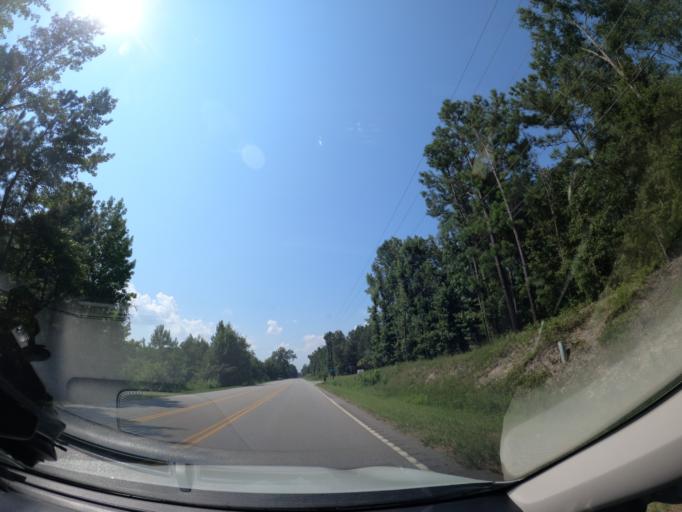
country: US
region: South Carolina
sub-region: Richland County
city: Hopkins
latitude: 33.9193
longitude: -80.9515
